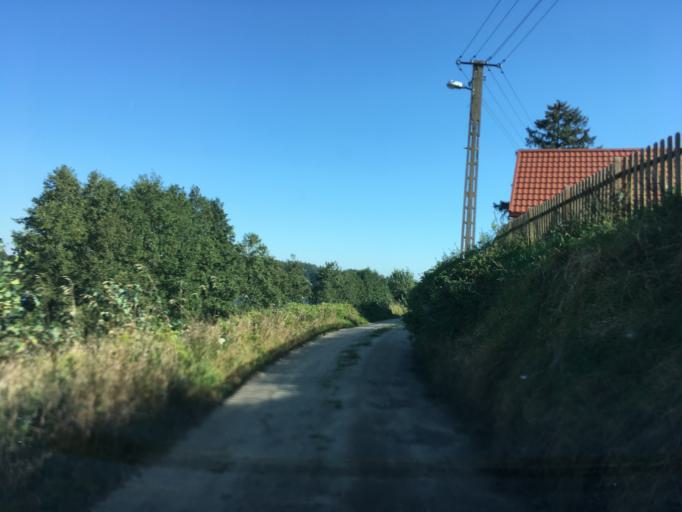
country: PL
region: Warmian-Masurian Voivodeship
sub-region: Powiat dzialdowski
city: Rybno
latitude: 53.3922
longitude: 19.8371
